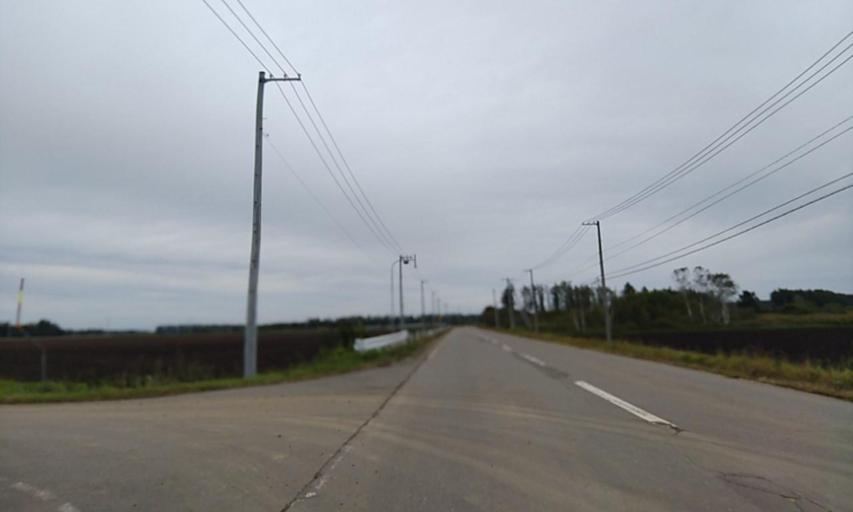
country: JP
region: Hokkaido
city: Obihiro
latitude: 42.6204
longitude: 143.2599
